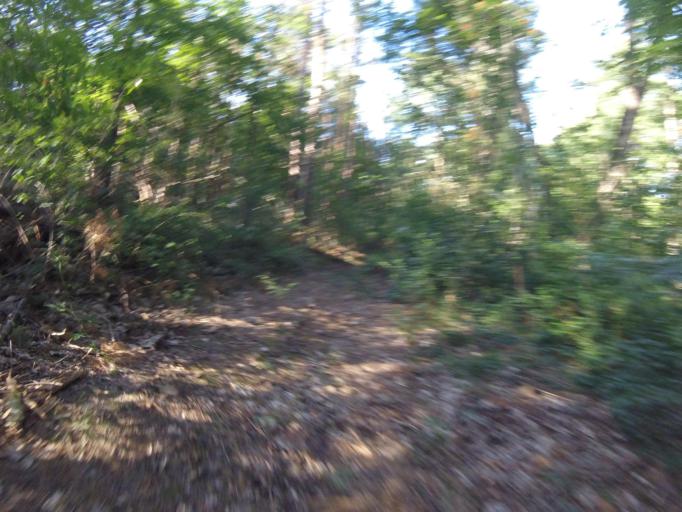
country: DE
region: Brandenburg
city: Wildau
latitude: 52.3232
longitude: 13.7236
